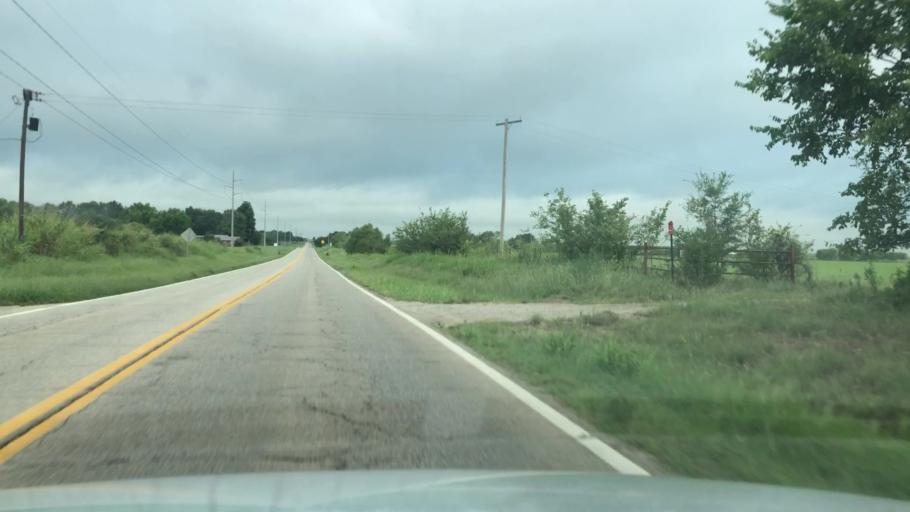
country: US
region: Oklahoma
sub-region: Nowata County
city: Nowata
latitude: 36.7136
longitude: -95.6746
